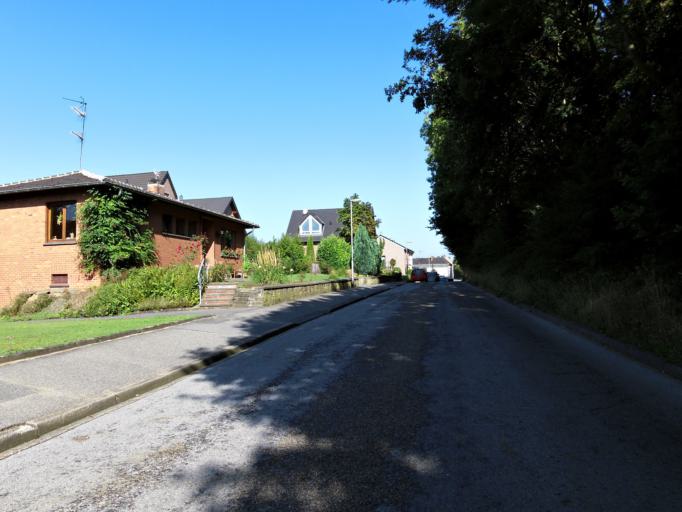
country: DE
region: North Rhine-Westphalia
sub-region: Regierungsbezirk Koln
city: Herzogenrath
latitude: 50.8814
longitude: 6.0865
